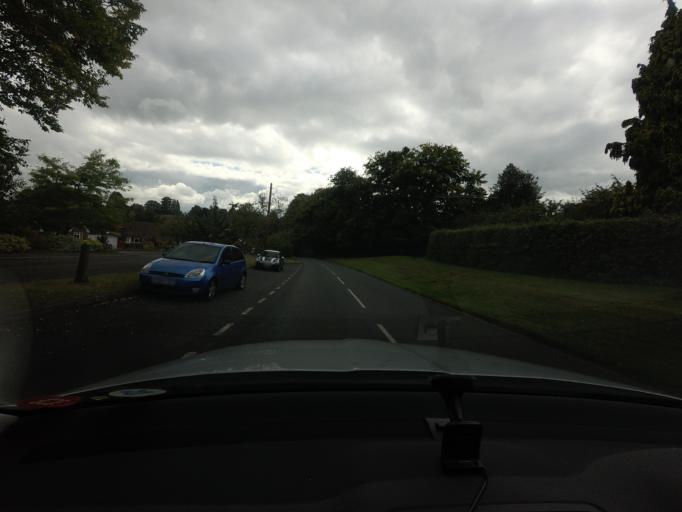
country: GB
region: England
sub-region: Kent
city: Borough Green
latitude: 51.2891
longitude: 0.2867
